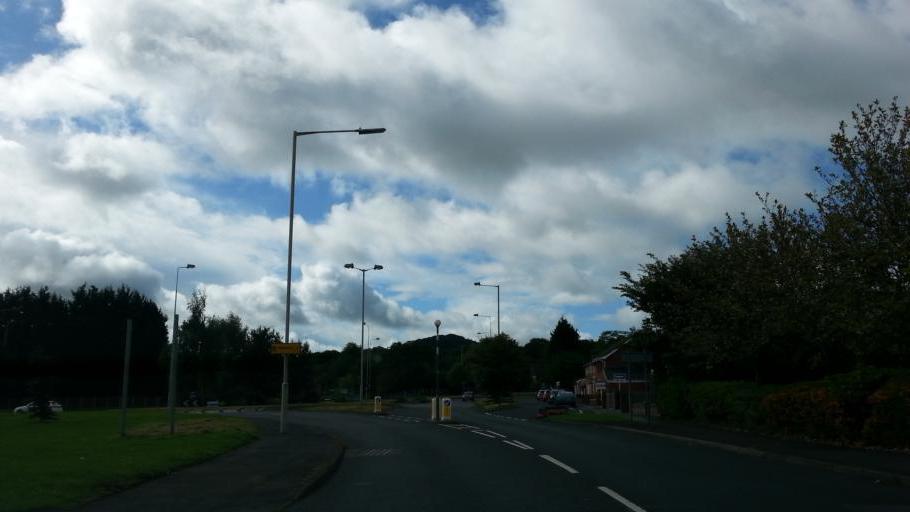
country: GB
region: England
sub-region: Dudley
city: Halesowen
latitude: 52.4378
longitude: -2.0767
